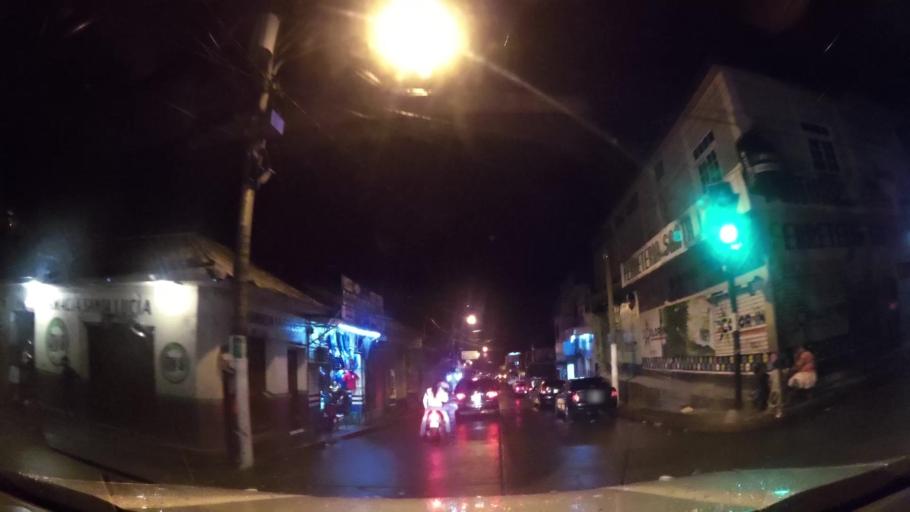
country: GT
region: Escuintla
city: Santa Lucia Cotzumalguapa
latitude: 14.3308
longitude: -91.0243
